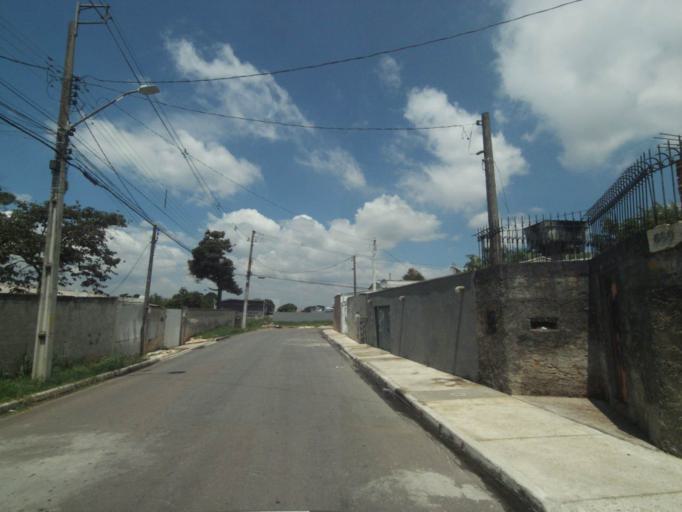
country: BR
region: Parana
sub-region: Pinhais
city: Pinhais
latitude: -25.4765
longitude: -49.1910
